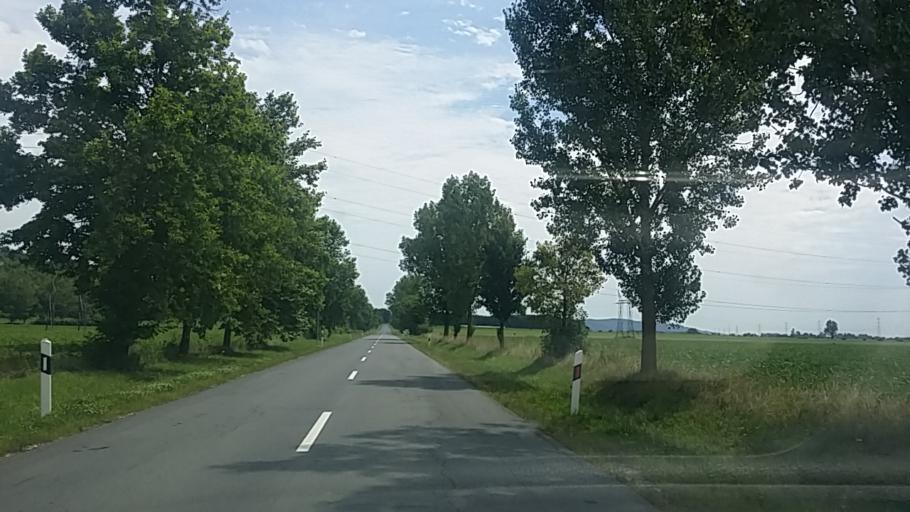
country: HR
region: Medimurska
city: Podturen
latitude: 46.5158
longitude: 16.5882
